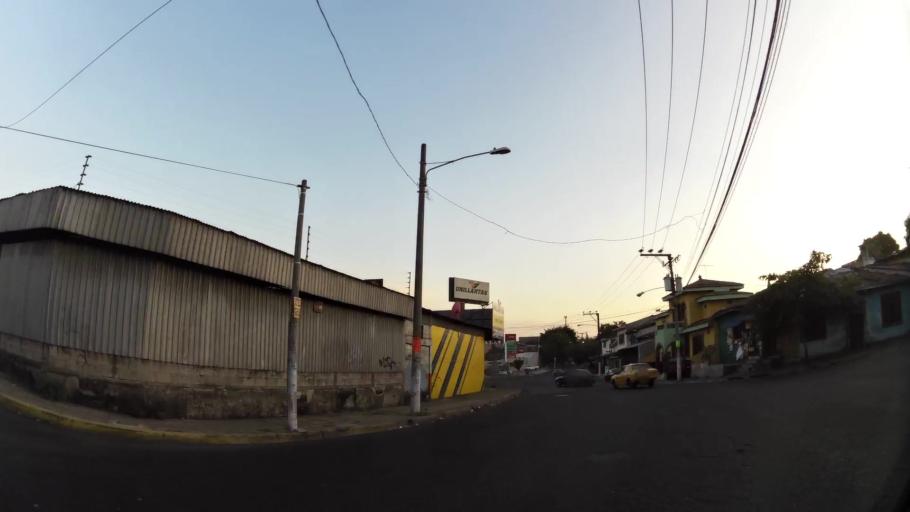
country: SV
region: San Salvador
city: Delgado
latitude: 13.7163
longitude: -89.1898
